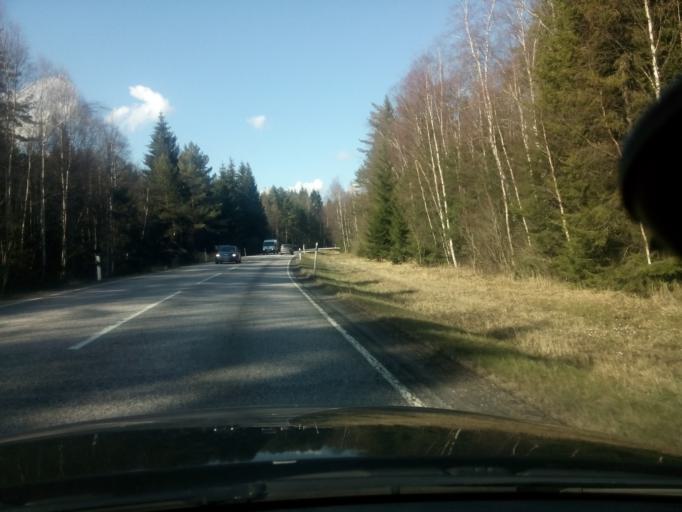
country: SE
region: Soedermanland
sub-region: Flens Kommun
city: Malmkoping
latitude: 59.2015
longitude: 16.7902
